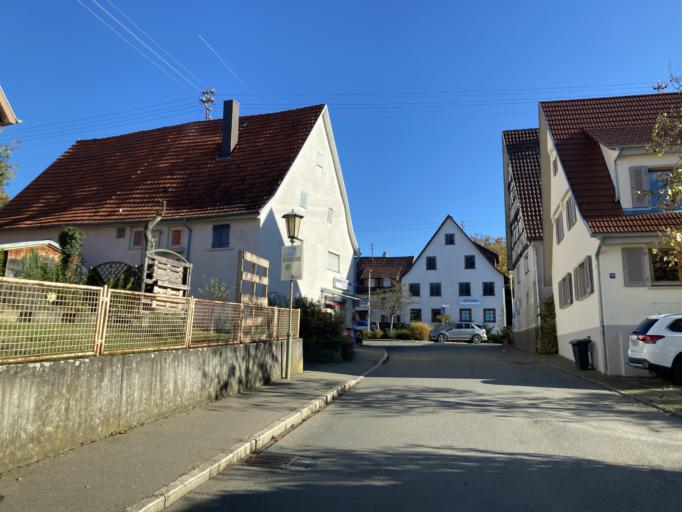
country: DE
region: Baden-Wuerttemberg
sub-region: Tuebingen Region
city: Mossingen
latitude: 48.3944
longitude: 9.0404
